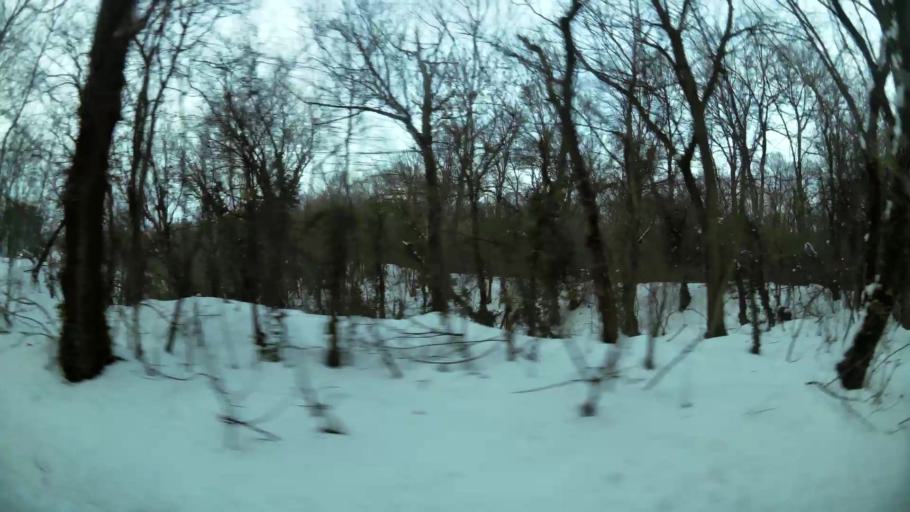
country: RS
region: Central Serbia
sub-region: Belgrade
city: Palilula
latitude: 44.8022
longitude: 20.5045
